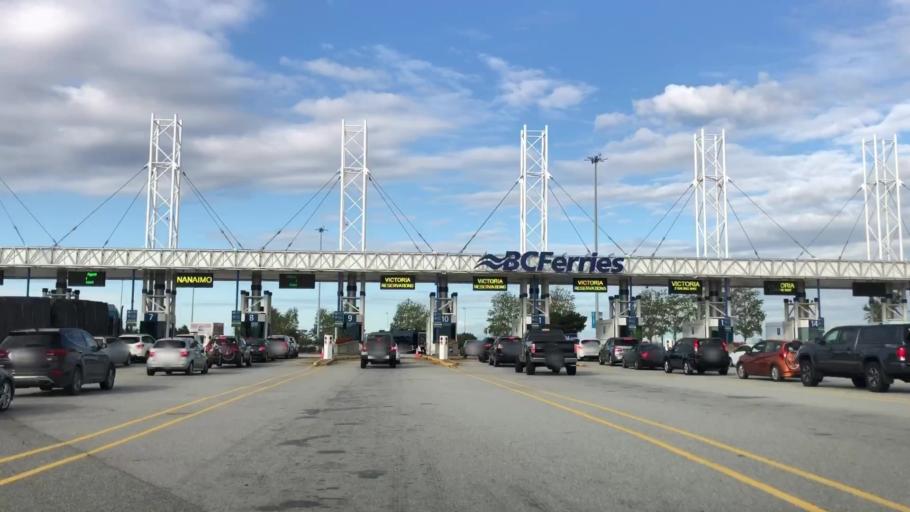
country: US
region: Washington
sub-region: Whatcom County
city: Point Roberts
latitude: 49.0107
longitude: -123.1256
